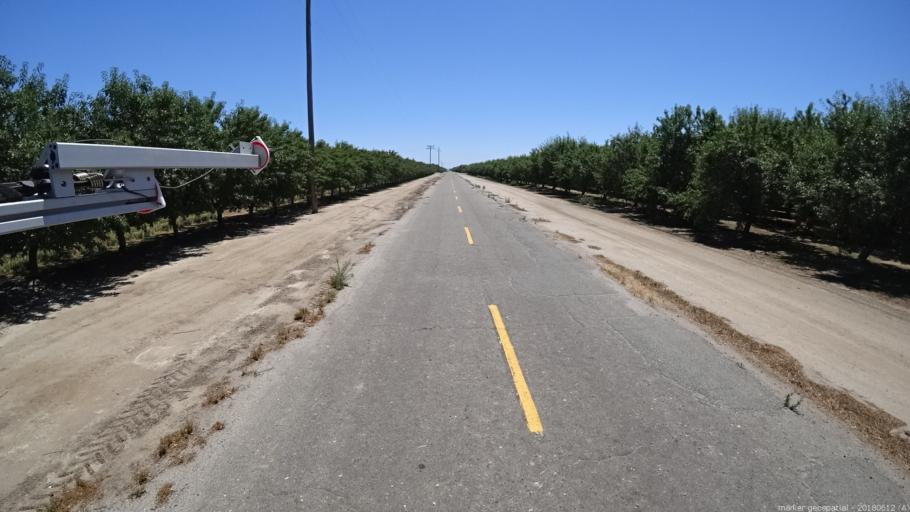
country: US
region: California
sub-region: Madera County
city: Chowchilla
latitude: 37.0565
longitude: -120.2745
